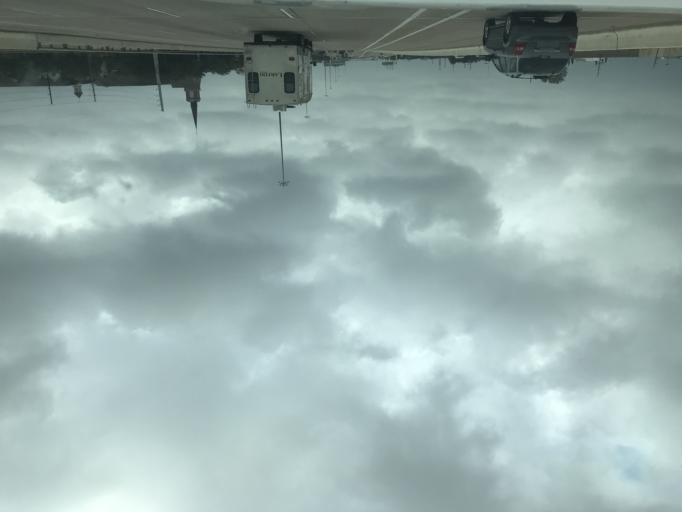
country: US
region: Texas
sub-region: Fort Bend County
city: Sugar Land
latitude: 29.5854
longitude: -95.6409
